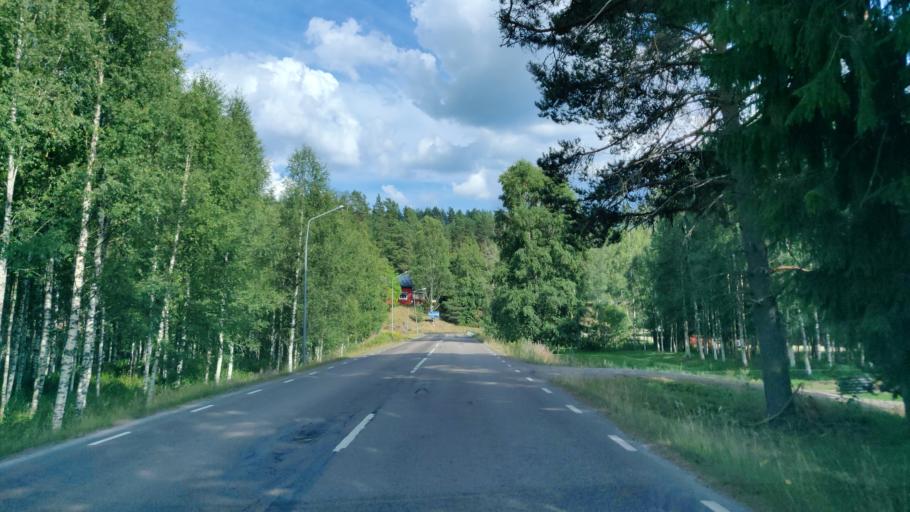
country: SE
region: Vaermland
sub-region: Hagfors Kommun
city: Ekshaerad
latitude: 60.1767
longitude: 13.5256
